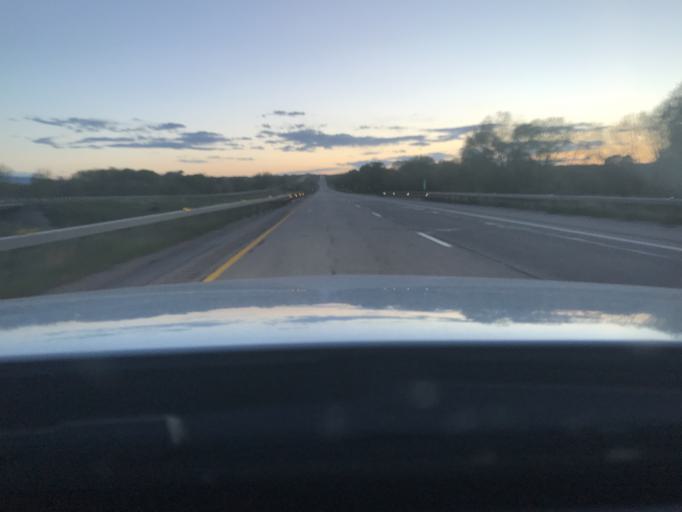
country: US
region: Wyoming
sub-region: Converse County
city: Glenrock
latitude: 42.8374
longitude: -105.8664
